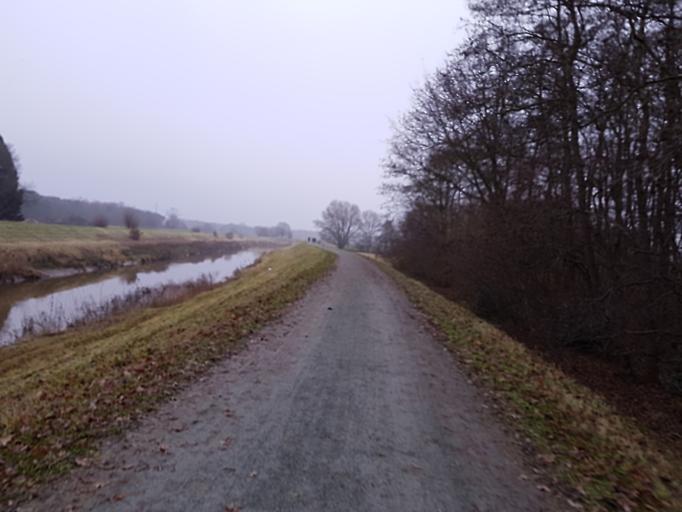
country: BE
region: Flanders
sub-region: Provincie Vlaams-Brabant
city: Keerbergen
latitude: 50.9921
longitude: 4.6152
